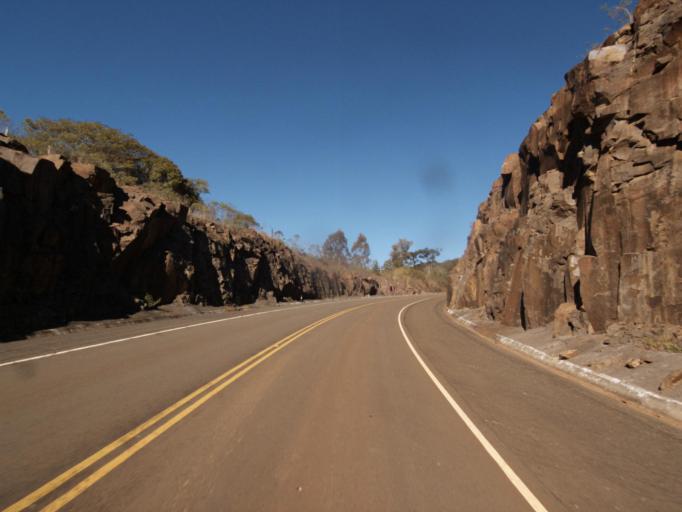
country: AR
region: Misiones
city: Bernardo de Irigoyen
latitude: -26.6096
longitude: -53.7269
